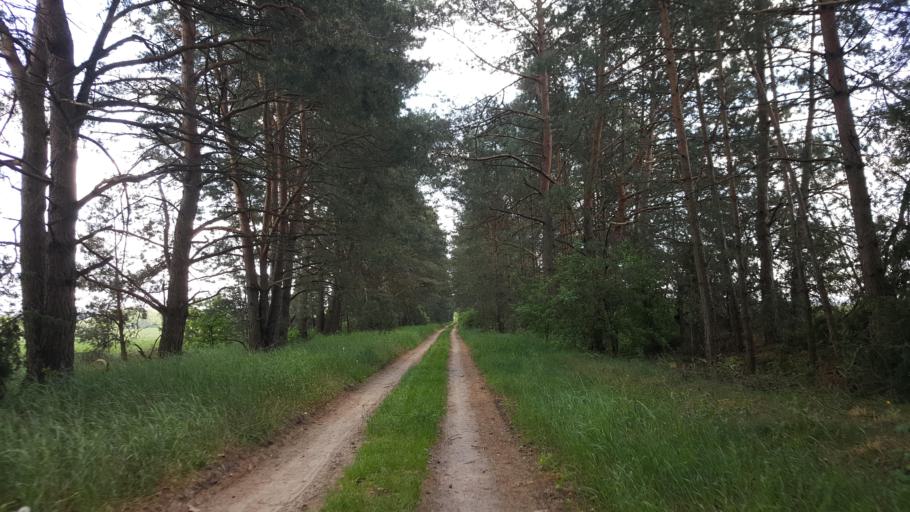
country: BY
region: Brest
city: Kamyanyets
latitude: 52.3928
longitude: 23.8725
